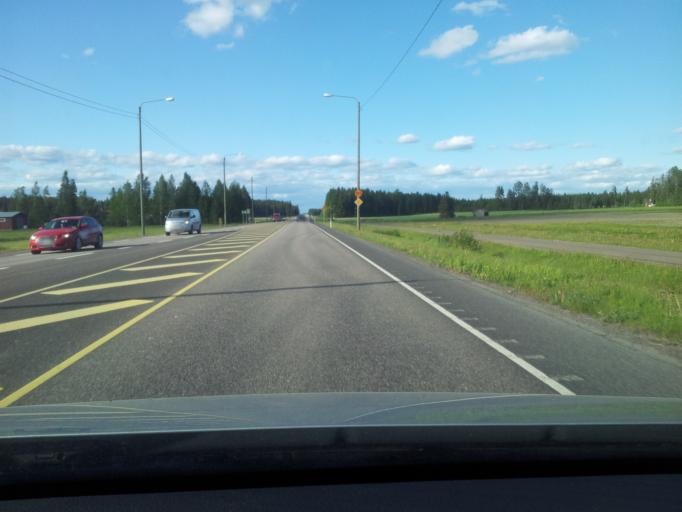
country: FI
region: Kymenlaakso
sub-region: Kouvola
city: Elimaeki
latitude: 60.7727
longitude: 26.4805
